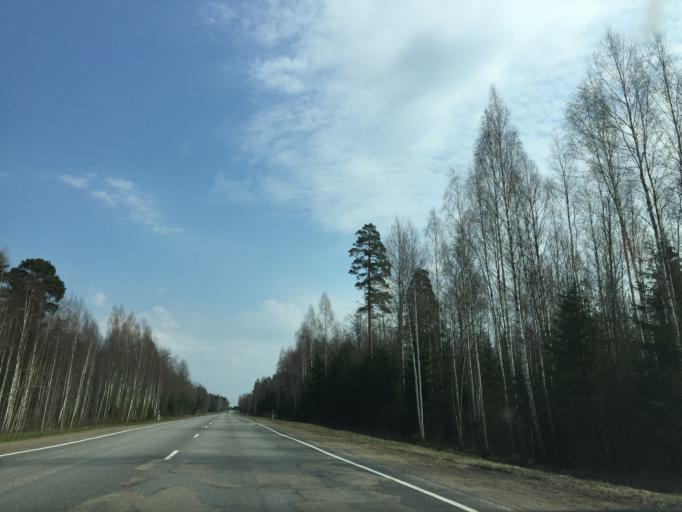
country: LV
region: Apes Novads
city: Ape
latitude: 57.4755
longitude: 26.4873
